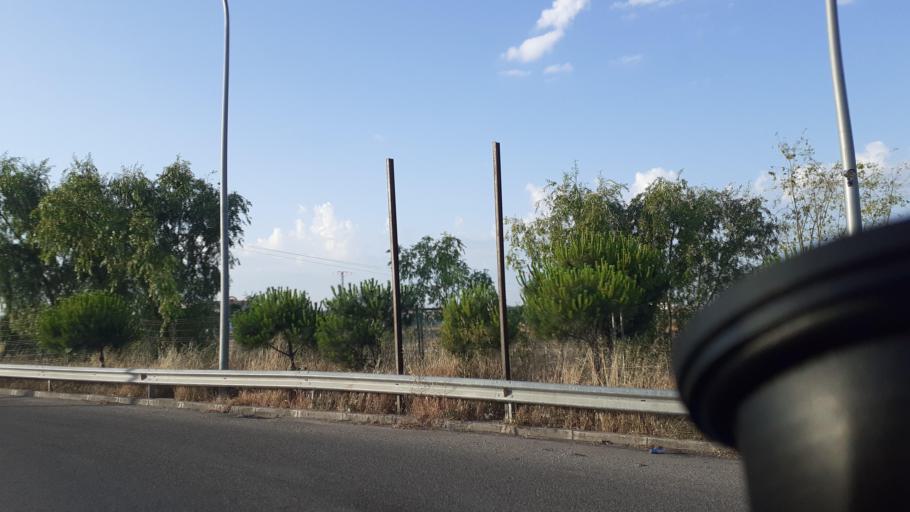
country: ES
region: Madrid
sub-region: Provincia de Madrid
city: El Molar
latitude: 40.7159
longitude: -3.5790
